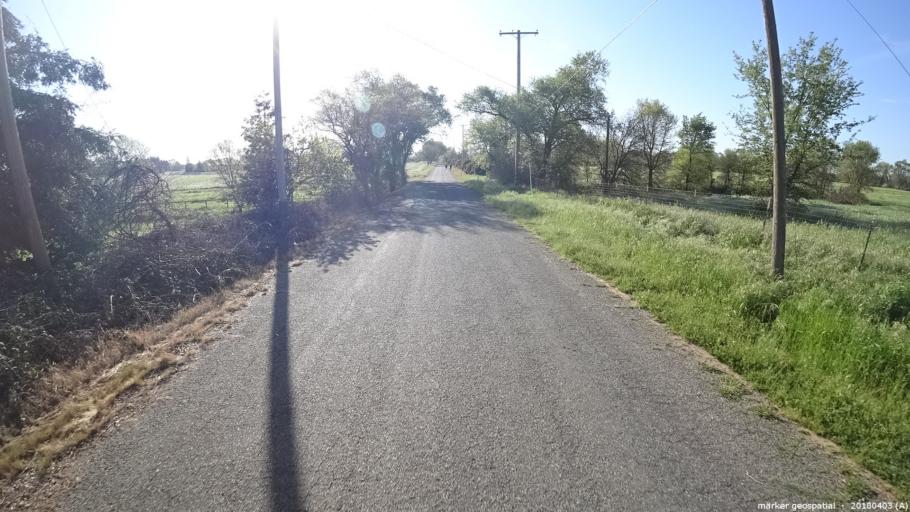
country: US
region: California
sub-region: Sacramento County
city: Wilton
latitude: 38.4395
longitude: -121.2084
